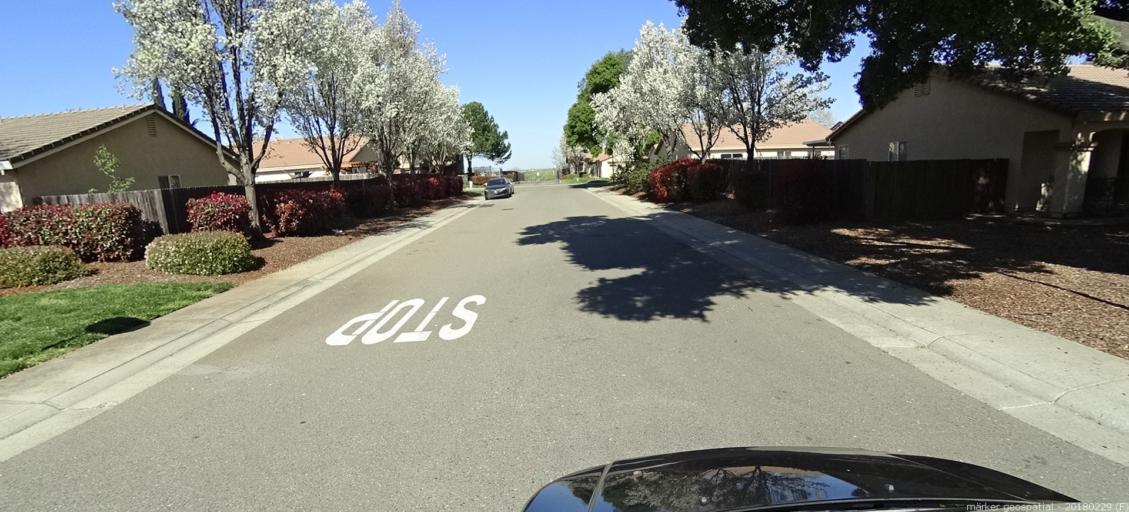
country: US
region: California
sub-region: Sacramento County
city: Rancho Cordova
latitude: 38.5468
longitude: -121.2857
